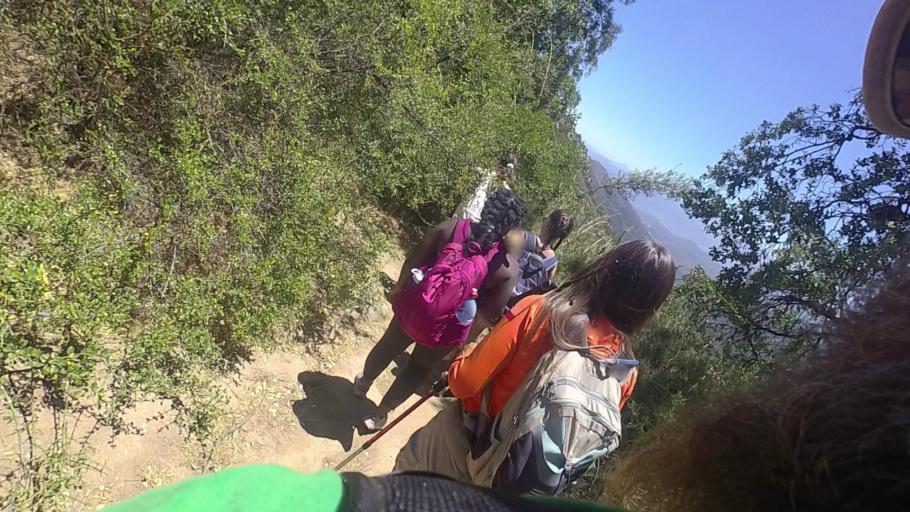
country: CL
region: Valparaiso
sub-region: Provincia de Quillota
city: Quillota
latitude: -32.9716
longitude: -71.0921
